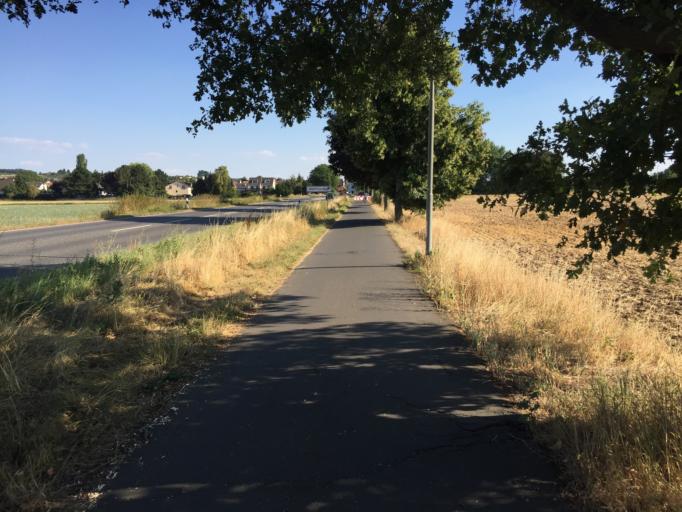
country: DE
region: Hesse
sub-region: Regierungsbezirk Giessen
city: Langgons
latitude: 50.5333
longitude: 8.6756
